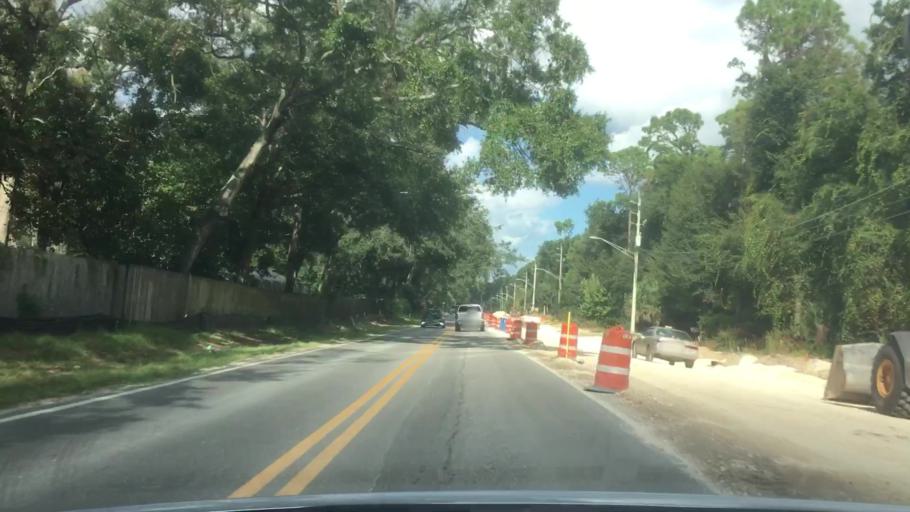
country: US
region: Florida
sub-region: Duval County
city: Atlantic Beach
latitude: 30.3480
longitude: -81.4610
